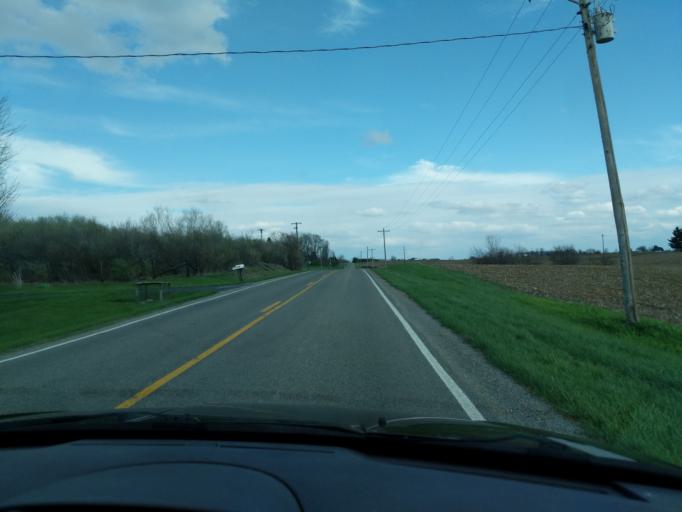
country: US
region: Ohio
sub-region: Champaign County
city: Urbana
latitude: 40.1531
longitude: -83.6500
